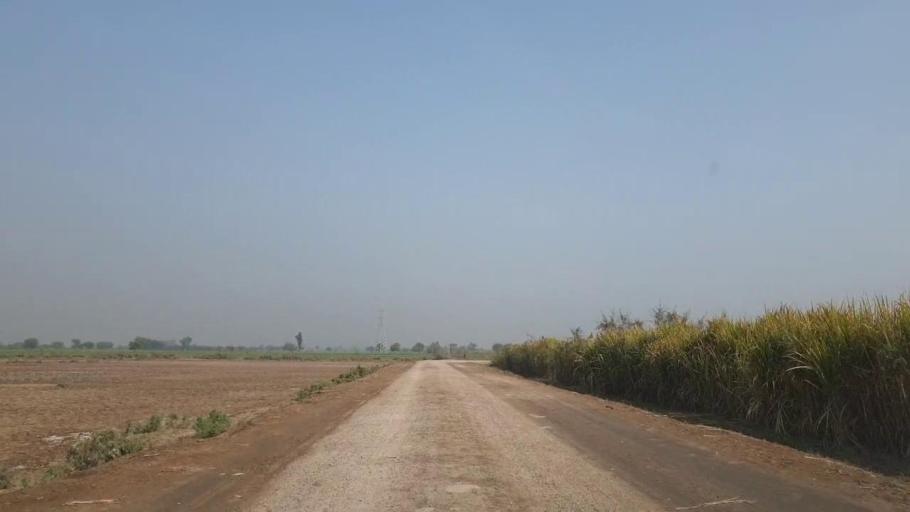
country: PK
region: Sindh
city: Mirpur Khas
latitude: 25.5624
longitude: 69.0109
